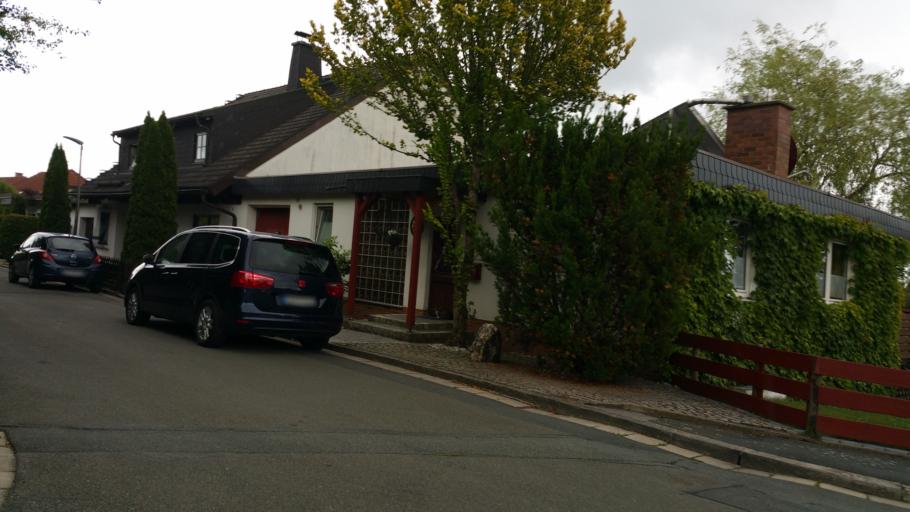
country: DE
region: Bavaria
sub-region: Upper Franconia
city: Rehau
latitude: 50.2555
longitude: 12.0346
